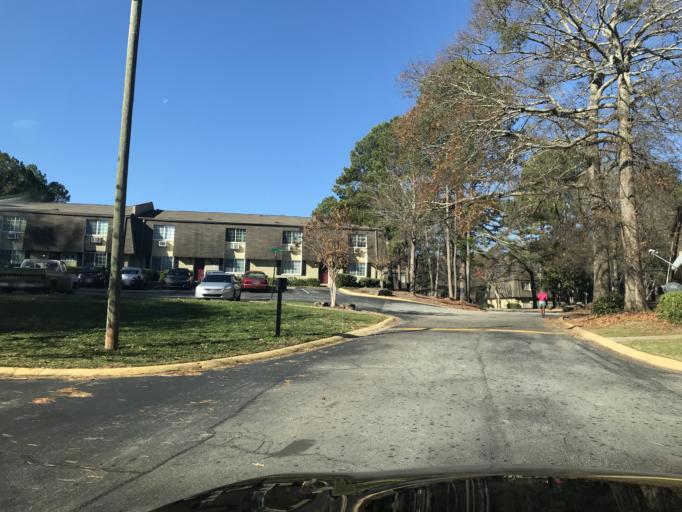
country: US
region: Georgia
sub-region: Clayton County
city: Morrow
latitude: 33.5702
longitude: -84.3668
